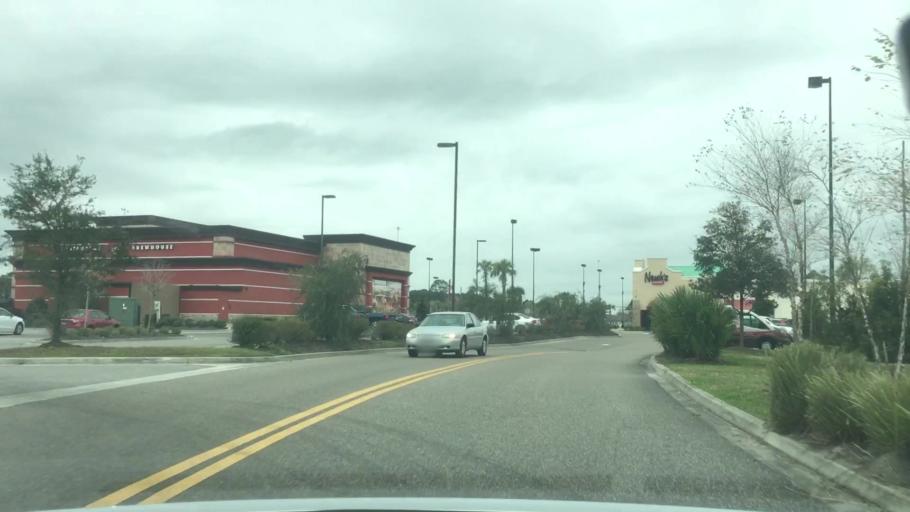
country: US
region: Florida
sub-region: Duval County
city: Jacksonville
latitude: 30.4827
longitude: -81.6382
